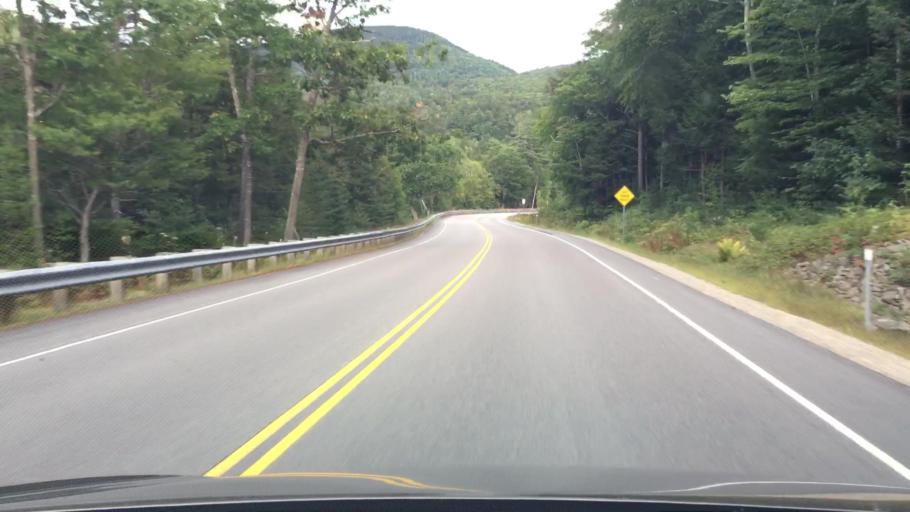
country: US
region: New Hampshire
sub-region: Carroll County
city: North Conway
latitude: 44.0167
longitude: -71.2504
